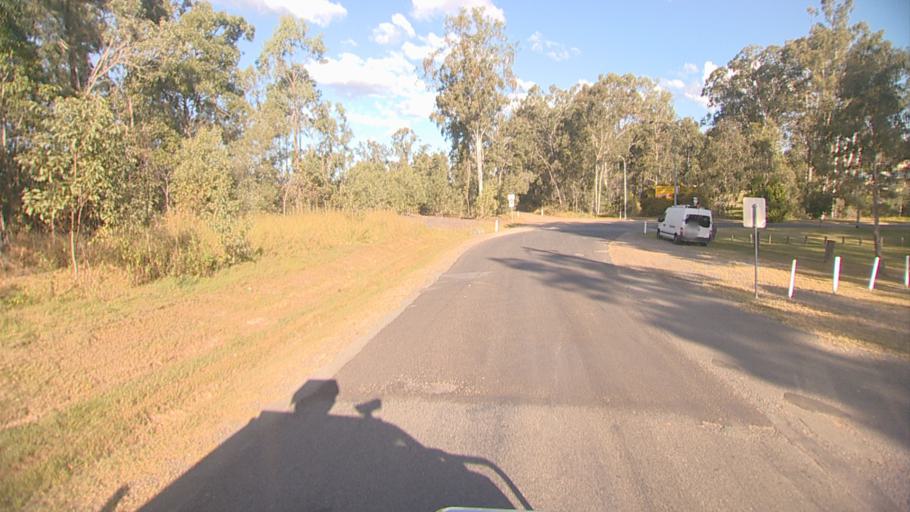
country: AU
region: Queensland
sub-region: Logan
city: North Maclean
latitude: -27.7478
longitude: 152.9409
